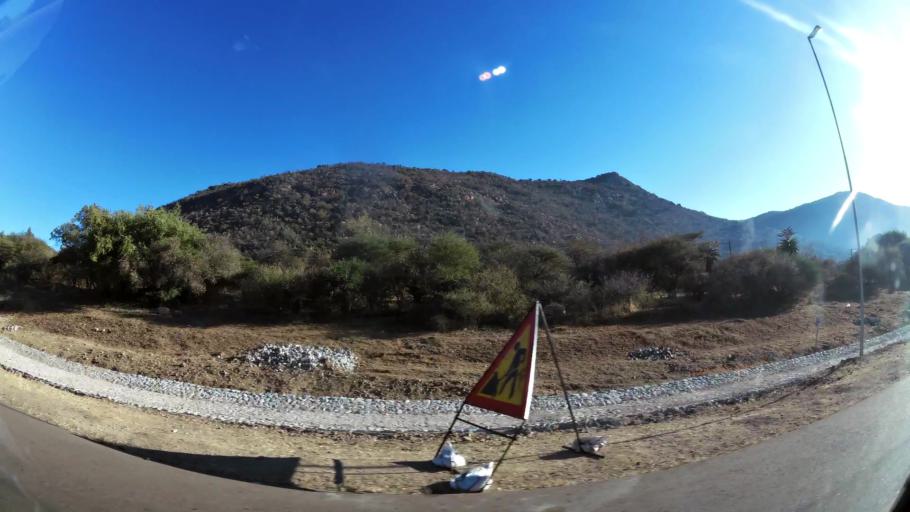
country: ZA
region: Limpopo
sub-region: Capricorn District Municipality
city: Mankoeng
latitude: -23.9451
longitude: 29.8040
